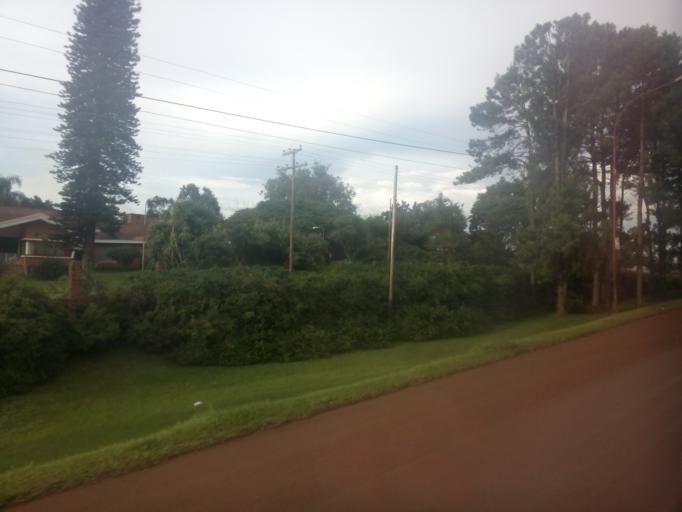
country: AR
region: Misiones
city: Guarani
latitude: -27.4906
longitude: -55.1506
